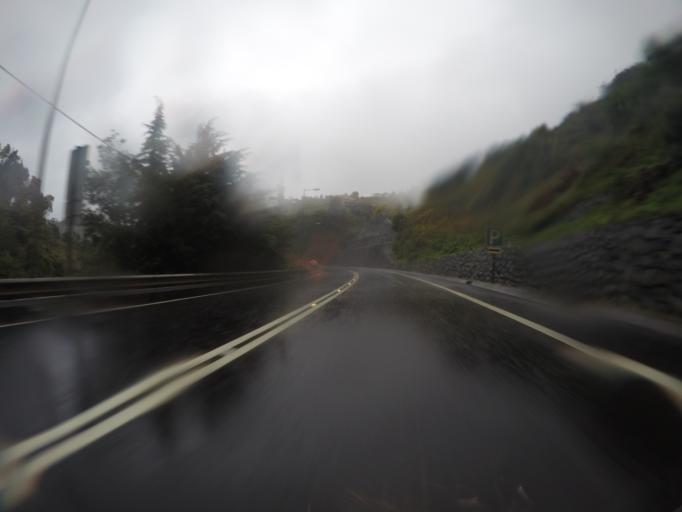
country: PT
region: Madeira
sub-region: Santana
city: Santana
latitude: 32.7644
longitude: -16.8355
